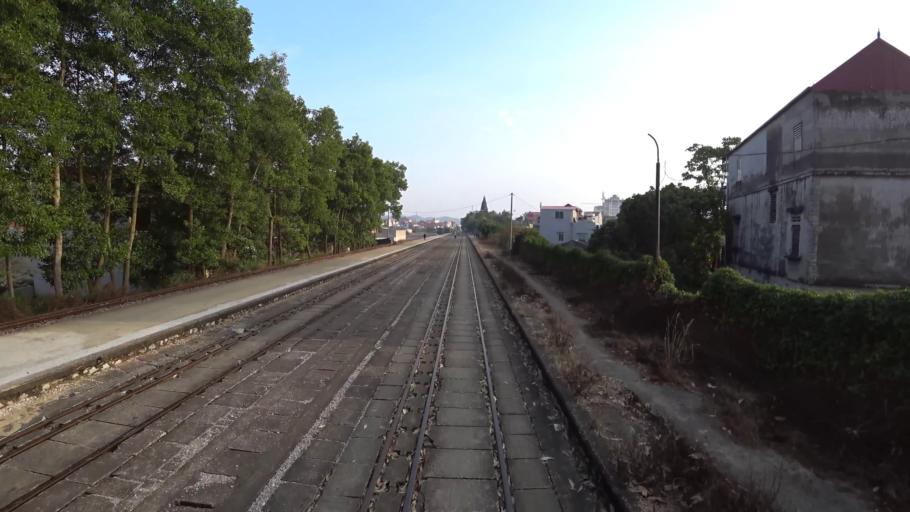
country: VN
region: Lang Son
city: Thi Tran Cao Loc
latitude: 21.8678
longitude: 106.7625
